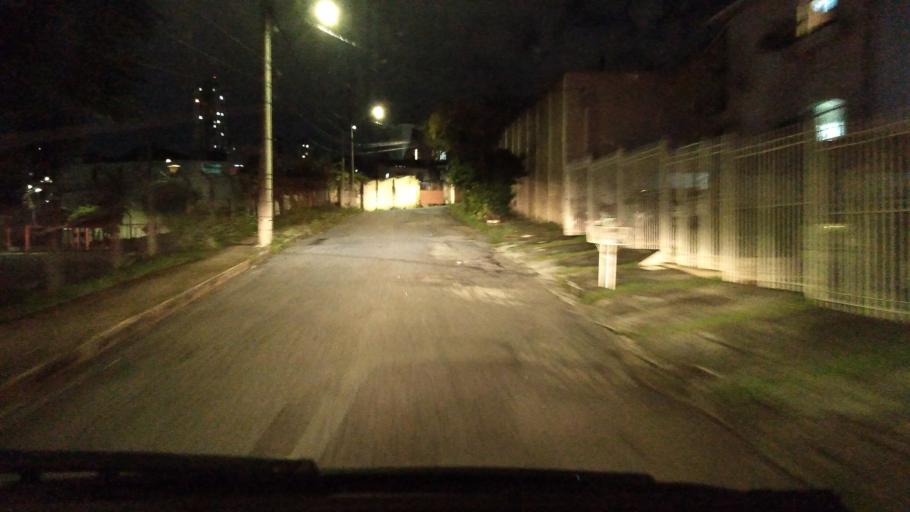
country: BR
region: Minas Gerais
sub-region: Belo Horizonte
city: Belo Horizonte
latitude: -19.8963
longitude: -43.9729
